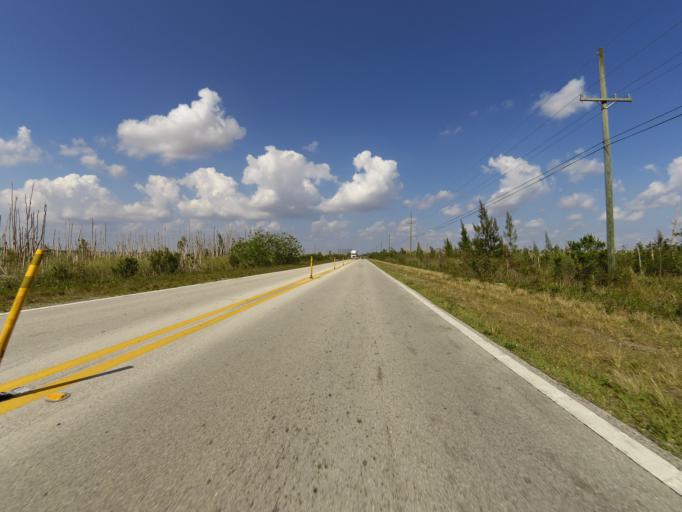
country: US
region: Florida
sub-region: Miami-Dade County
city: Palm Springs North
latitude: 25.9334
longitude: -80.4469
